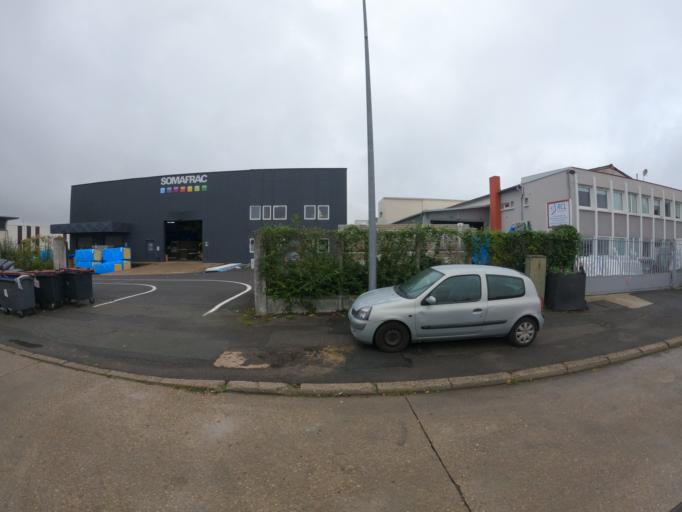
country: FR
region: Ile-de-France
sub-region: Departement du Val-de-Marne
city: Chennevieres-sur-Marne
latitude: 48.7965
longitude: 2.5446
